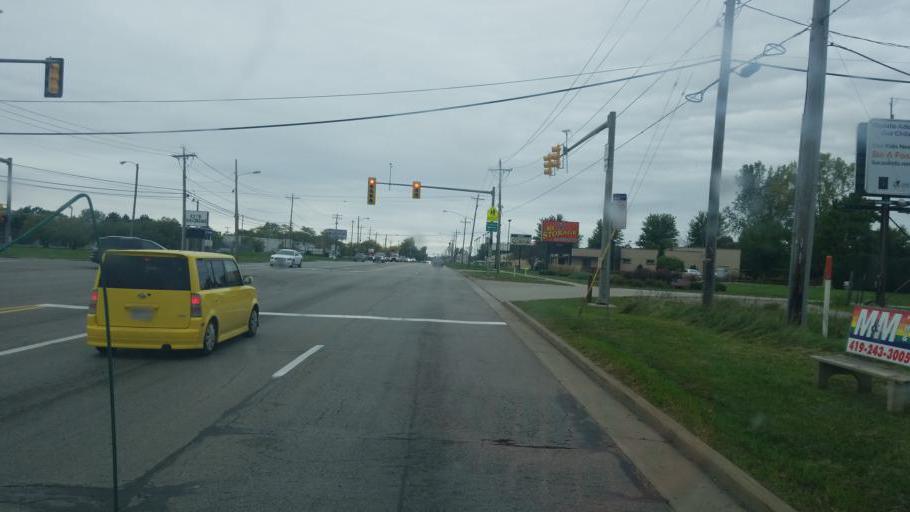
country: US
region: Ohio
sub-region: Lucas County
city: Ottawa Hills
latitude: 41.6266
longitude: -83.6644
